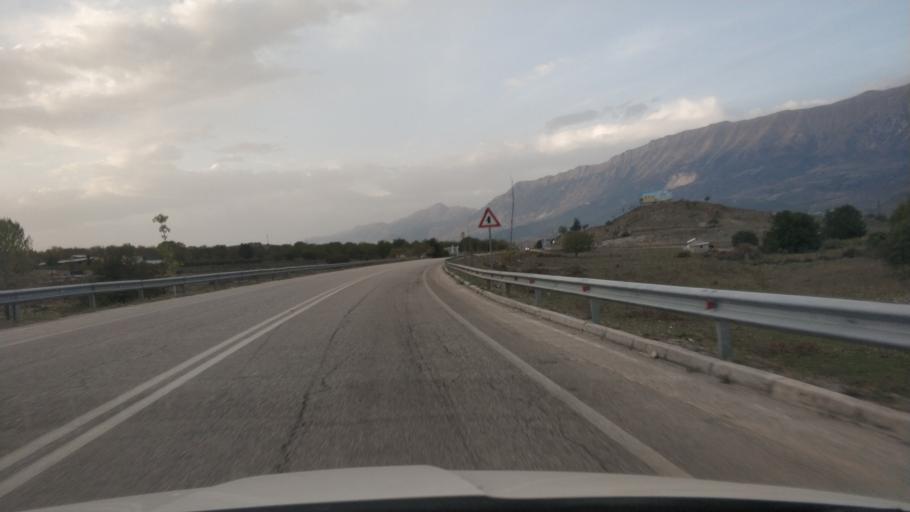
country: AL
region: Gjirokaster
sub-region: Rrethi i Gjirokastres
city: Dervician
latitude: 40.0412
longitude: 20.1761
